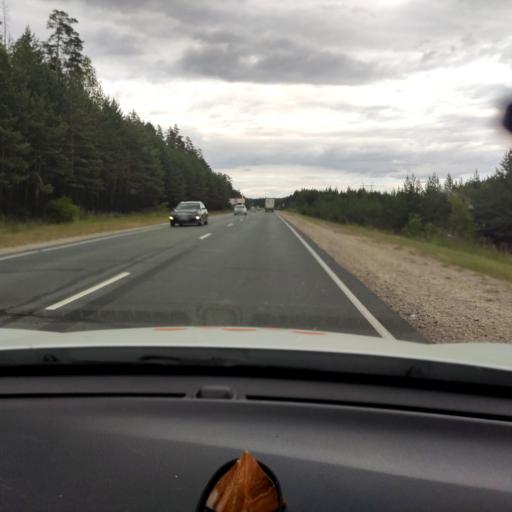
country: RU
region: Mariy-El
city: Volzhsk
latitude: 55.8982
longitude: 48.3898
